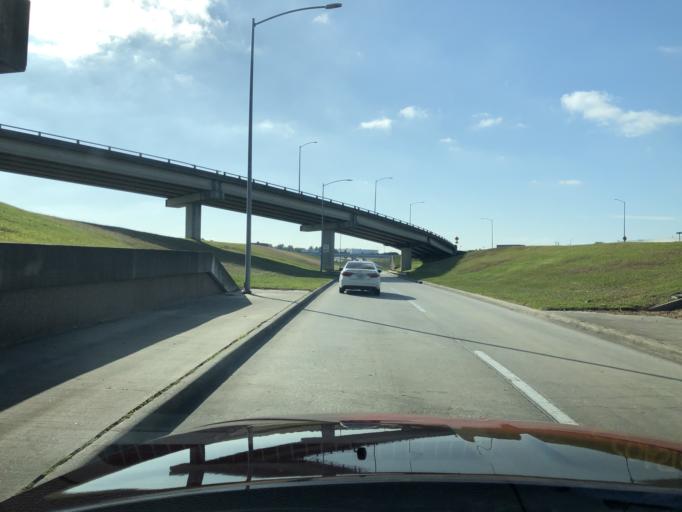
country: US
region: Texas
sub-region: Harris County
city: Aldine
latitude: 29.9820
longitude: -95.3428
